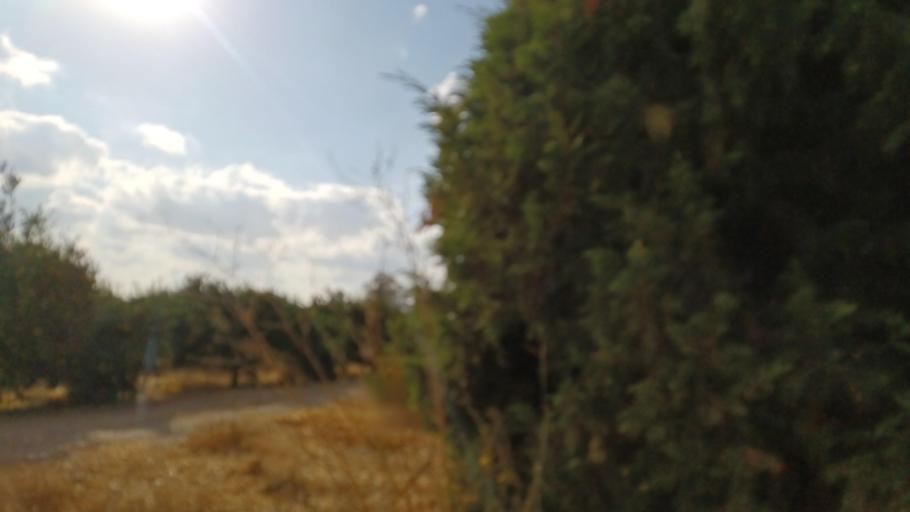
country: CY
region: Limassol
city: Pissouri
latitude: 34.7008
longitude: 32.5560
